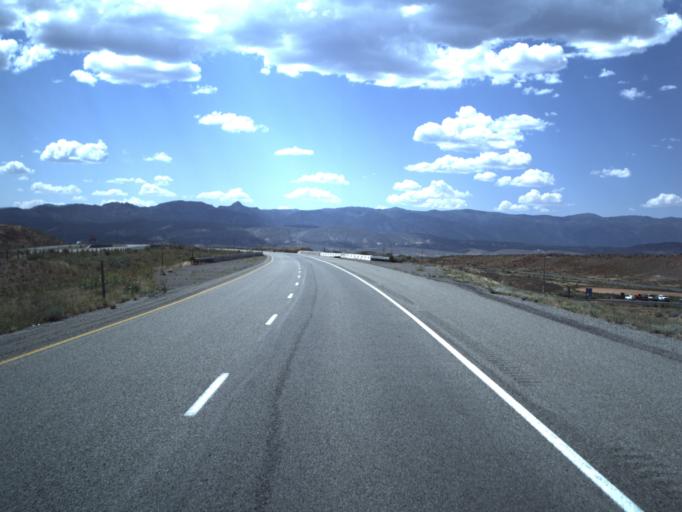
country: US
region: Utah
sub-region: Sevier County
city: Salina
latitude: 38.9338
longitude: -111.8519
